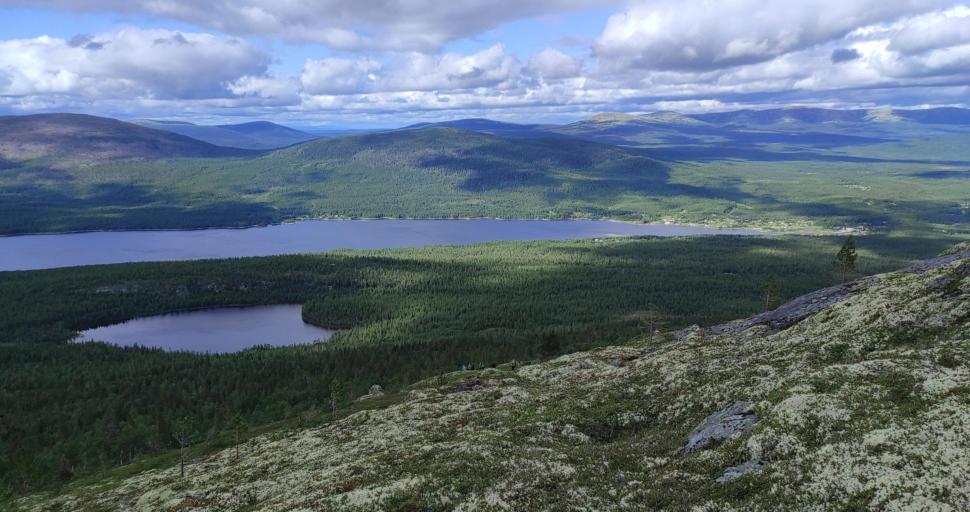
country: RU
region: Murmansk
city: Afrikanda
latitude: 67.0575
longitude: 32.9611
